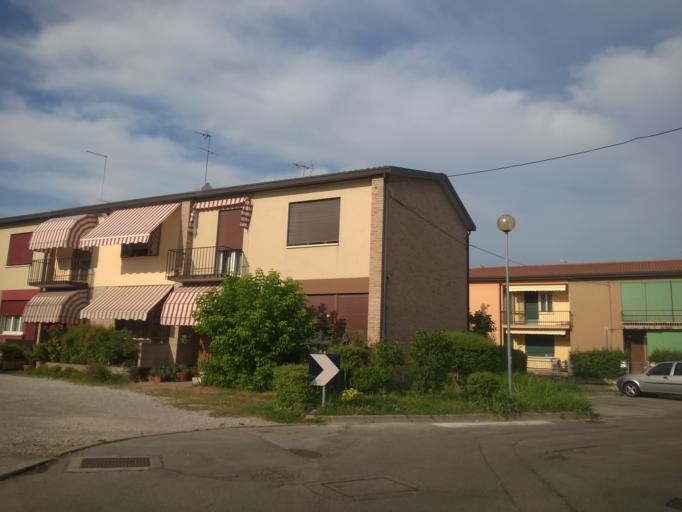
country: IT
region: Veneto
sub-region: Provincia di Padova
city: Piove di Sacco-Piovega
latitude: 45.2876
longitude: 12.0316
